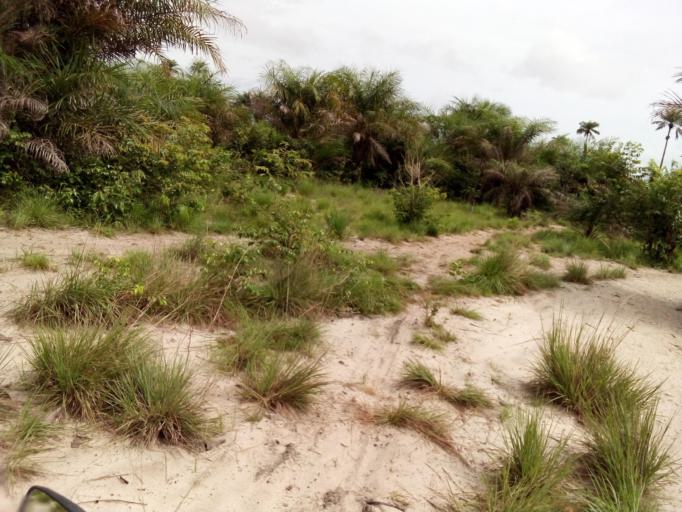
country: SL
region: Southern Province
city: Bonthe
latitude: 7.5175
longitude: -12.5707
